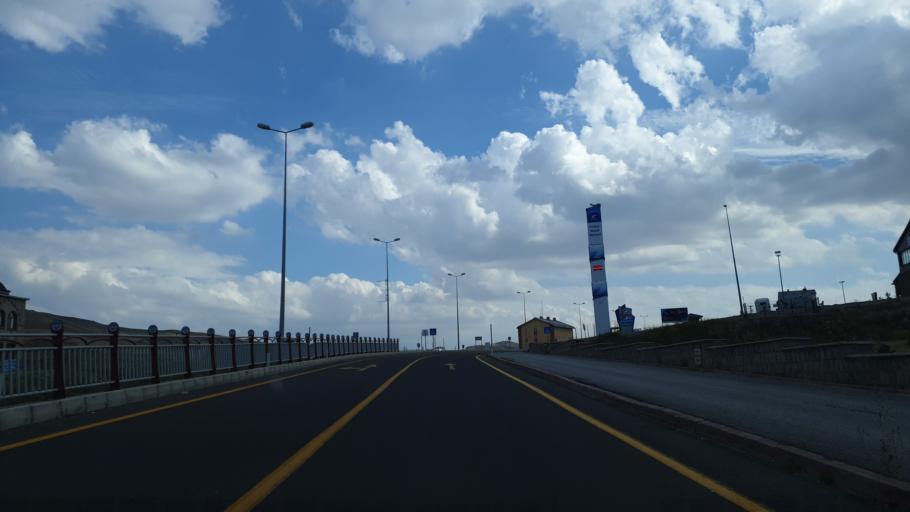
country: TR
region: Kayseri
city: Hacilar
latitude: 38.5412
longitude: 35.5277
